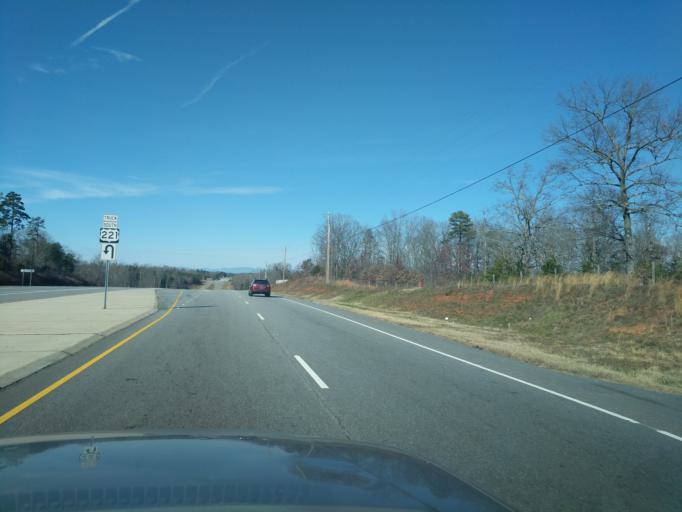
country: US
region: North Carolina
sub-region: Rutherford County
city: Forest City
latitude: 35.2969
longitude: -81.9127
